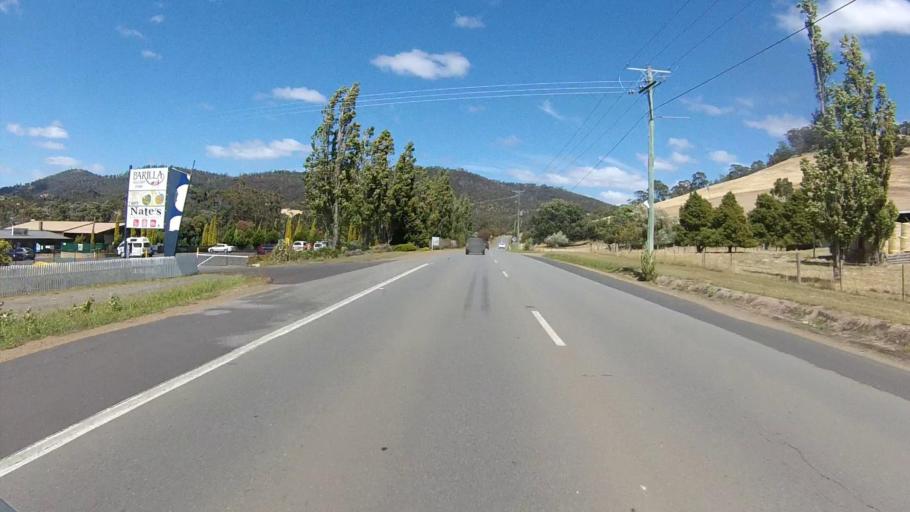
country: AU
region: Tasmania
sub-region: Clarence
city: Cambridge
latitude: -42.8320
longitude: 147.4444
